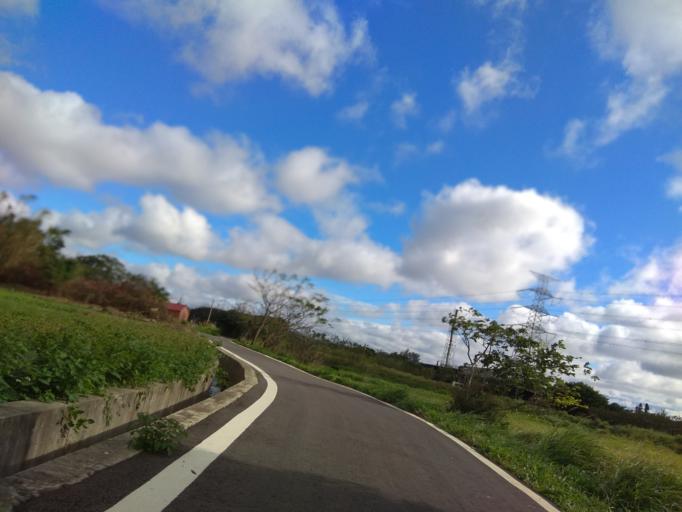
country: TW
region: Taiwan
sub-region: Hsinchu
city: Zhubei
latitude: 24.9692
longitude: 121.0810
